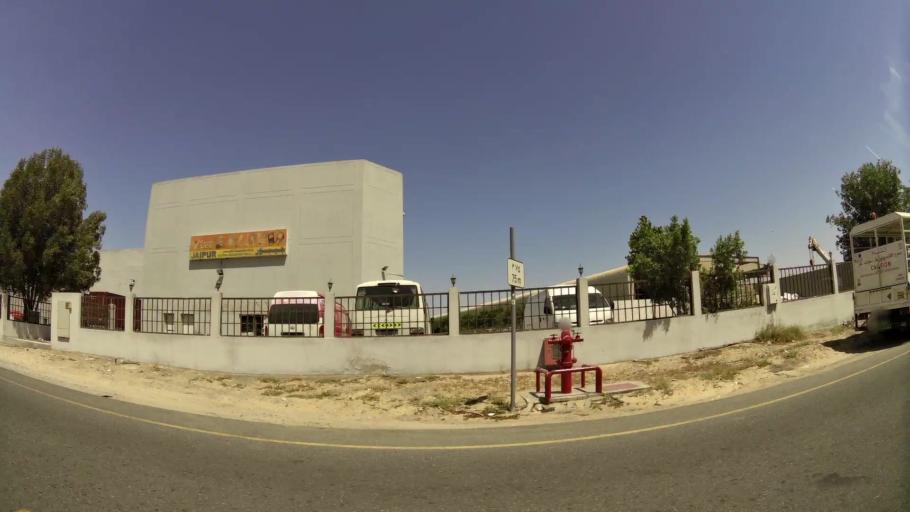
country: AE
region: Dubai
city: Dubai
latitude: 24.9849
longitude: 55.2116
